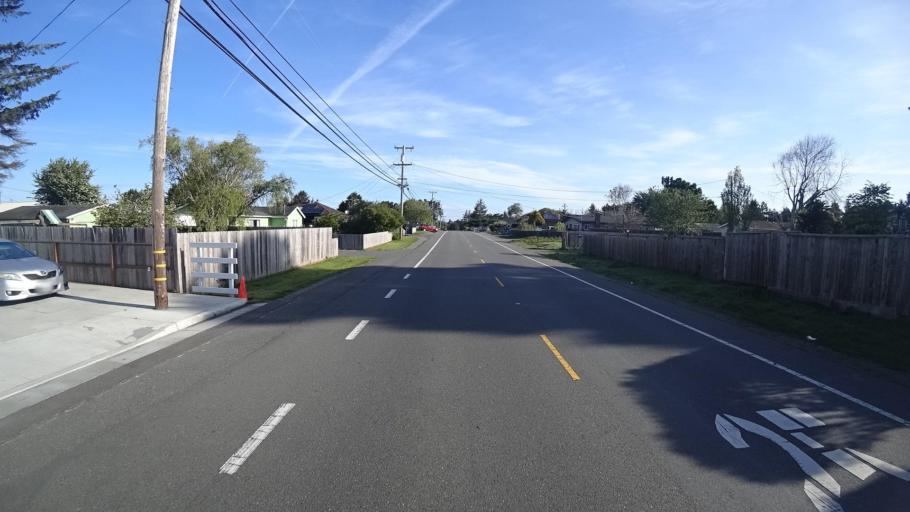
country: US
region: California
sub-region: Humboldt County
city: Bayview
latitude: 40.7639
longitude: -124.1755
